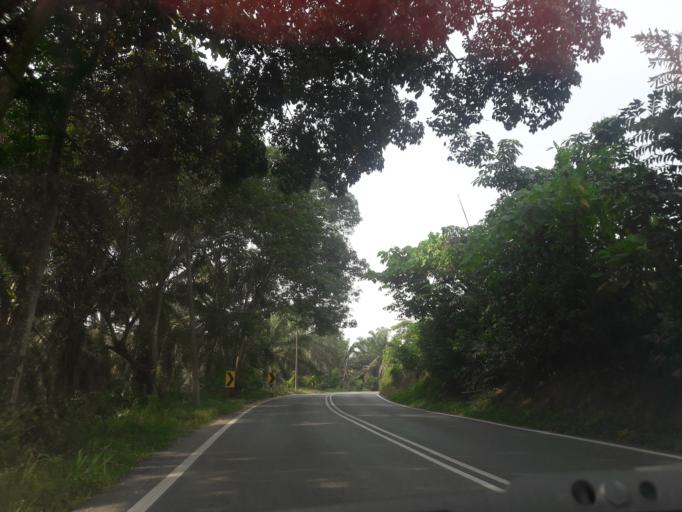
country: MY
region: Kedah
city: Kulim
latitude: 5.3586
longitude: 100.5209
